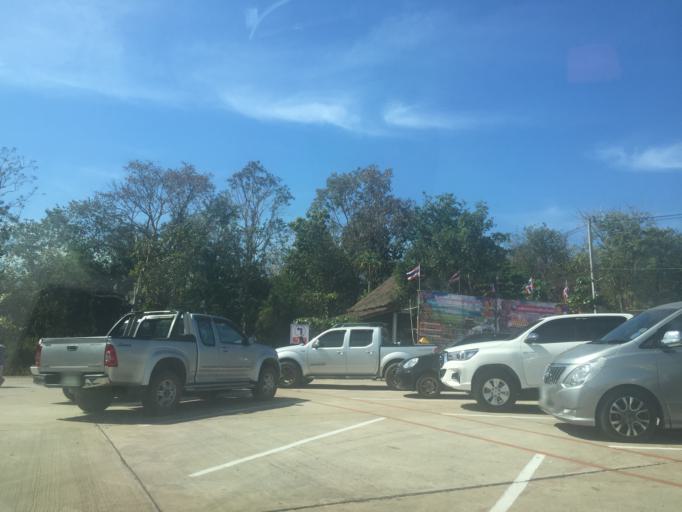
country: TH
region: Changwat Nong Bua Lamphu
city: Nong Bua Lamphu
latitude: 17.2440
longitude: 102.5153
